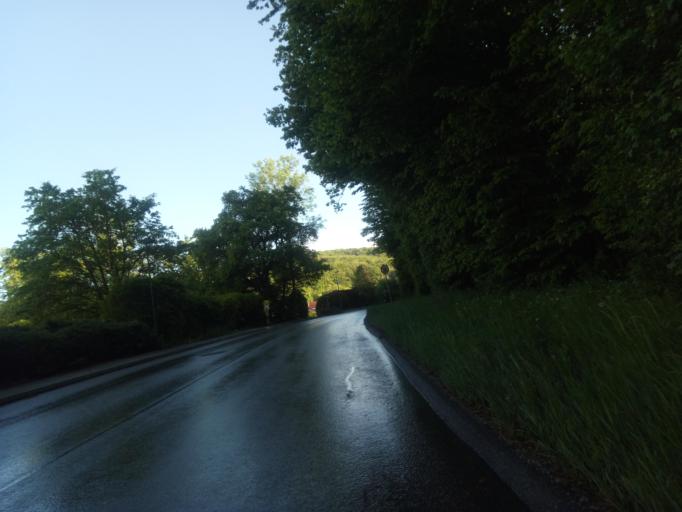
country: AT
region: Lower Austria
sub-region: Politischer Bezirk Modling
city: Kaltenleutgeben
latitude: 48.1333
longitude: 16.1938
